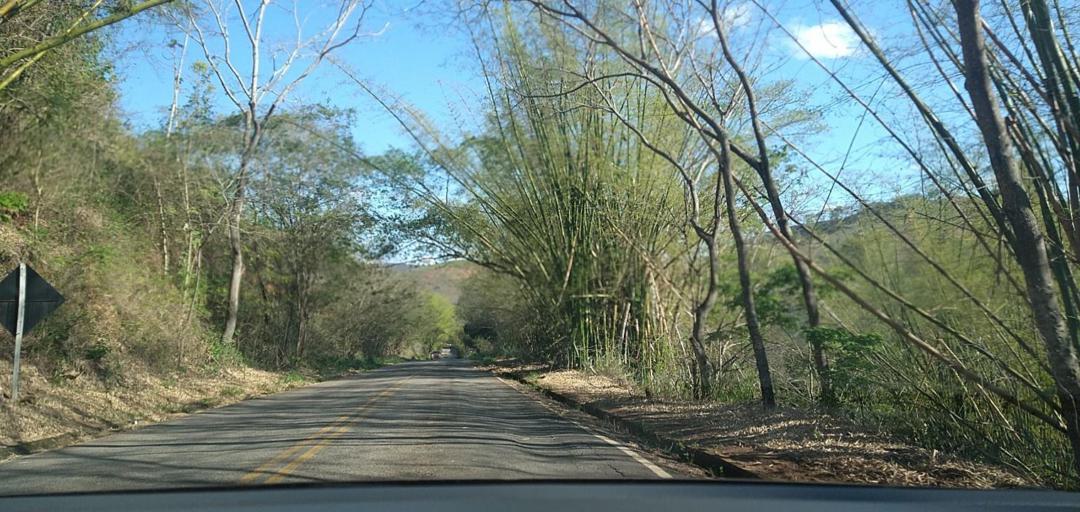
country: BR
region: Minas Gerais
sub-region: Ponte Nova
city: Ponte Nova
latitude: -20.2424
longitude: -42.8949
